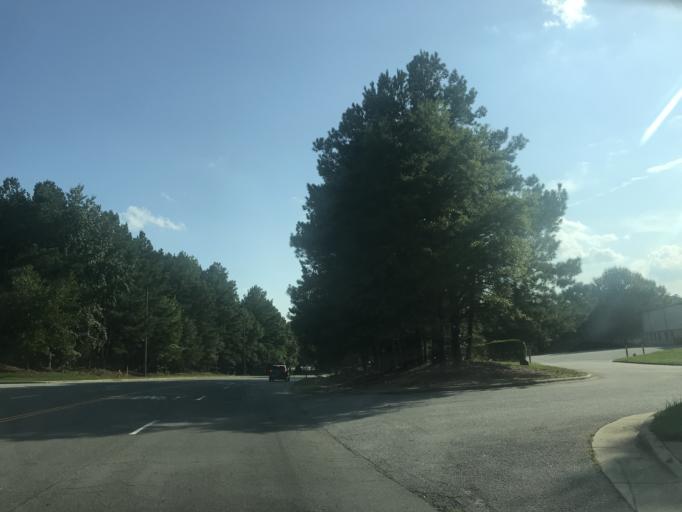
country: US
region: North Carolina
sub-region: Wake County
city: Knightdale
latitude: 35.7709
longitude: -78.5571
